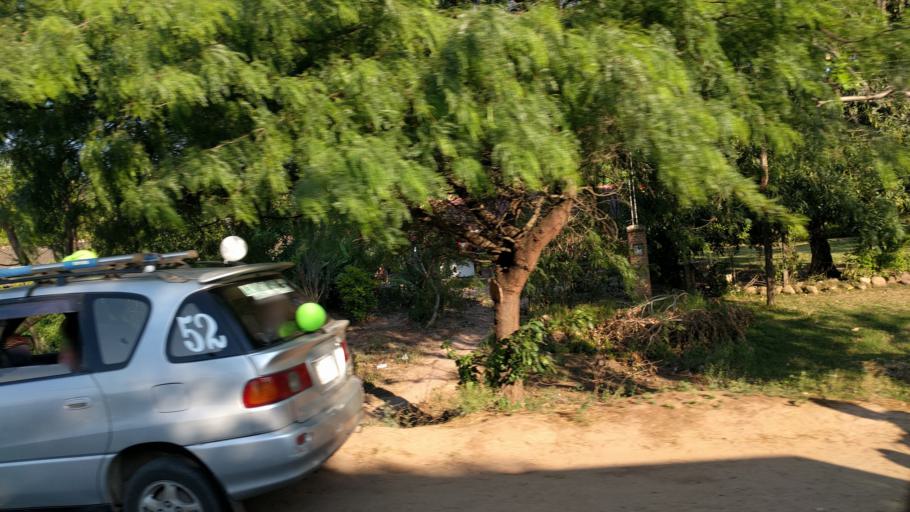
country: BO
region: Santa Cruz
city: Jorochito
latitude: -18.0636
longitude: -63.4346
